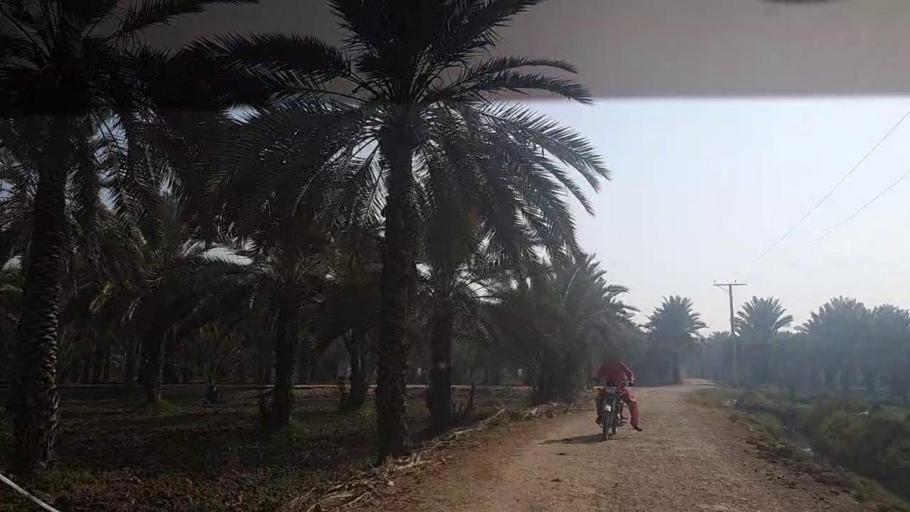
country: PK
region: Sindh
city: Khairpur
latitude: 27.4788
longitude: 68.7196
